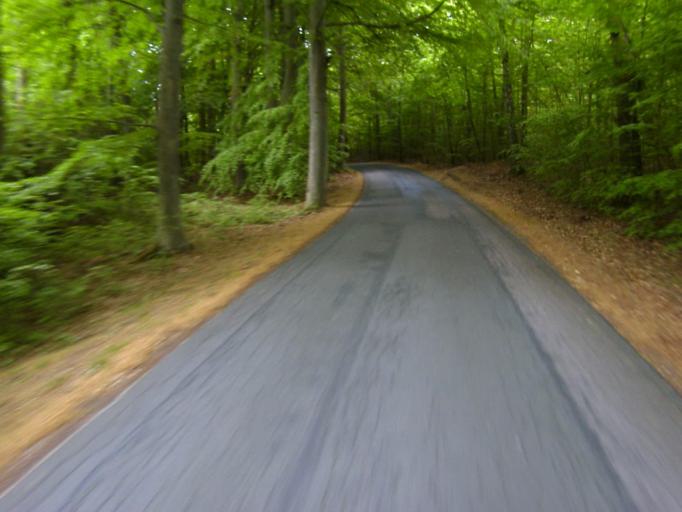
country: SE
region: Skane
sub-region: Kristianstads Kommun
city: Ahus
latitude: 55.9225
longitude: 14.3124
